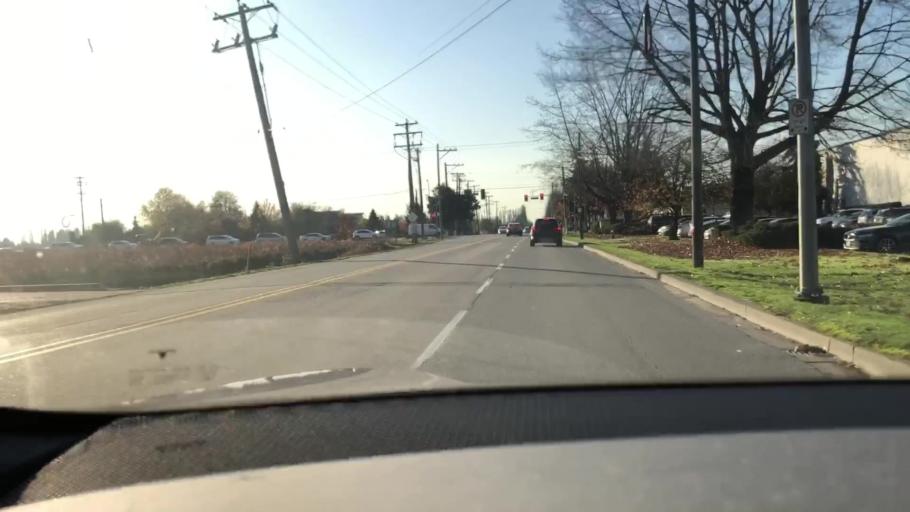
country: CA
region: British Columbia
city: Richmond
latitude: 49.1860
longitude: -123.0692
